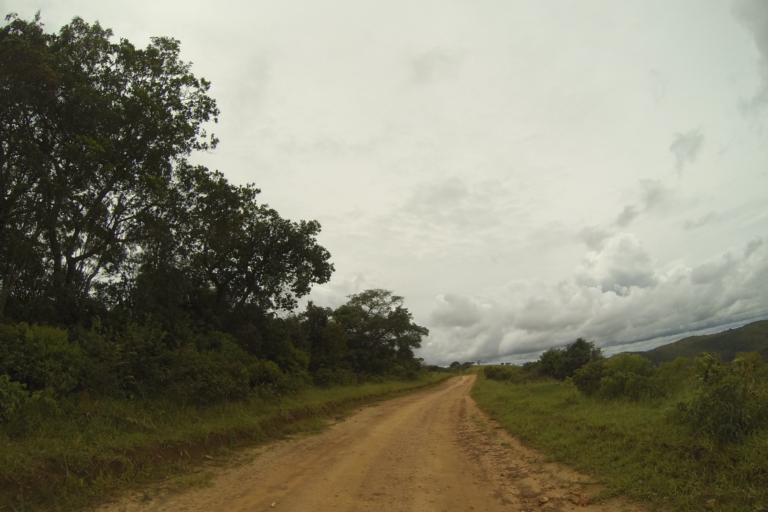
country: BR
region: Minas Gerais
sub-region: Ibia
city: Ibia
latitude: -19.6886
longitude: -46.6841
